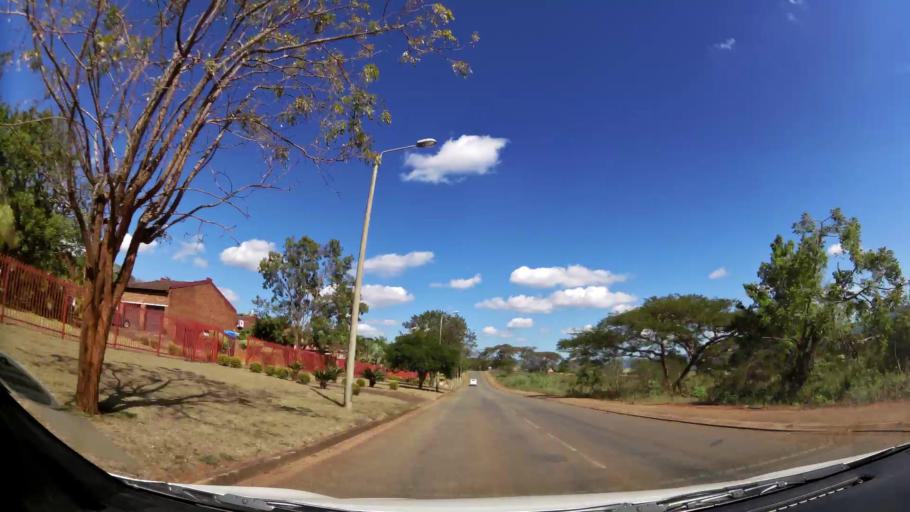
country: ZA
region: Limpopo
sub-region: Mopani District Municipality
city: Tzaneen
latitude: -23.8174
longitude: 30.1454
